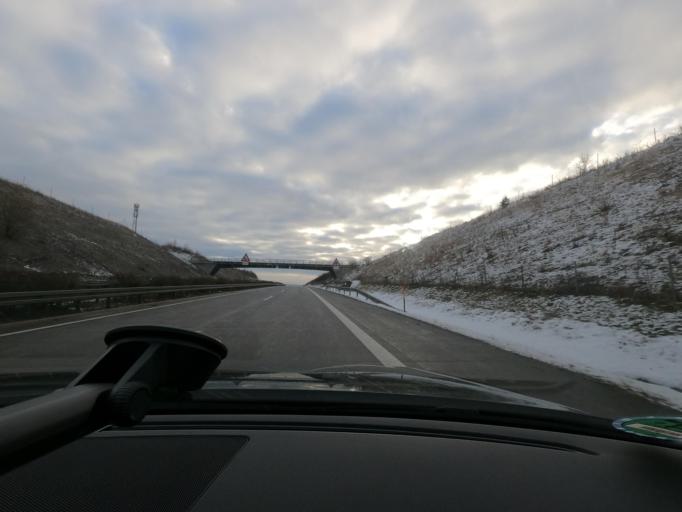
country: DE
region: Thuringia
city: Veilsdorf
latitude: 50.4662
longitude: 10.8367
